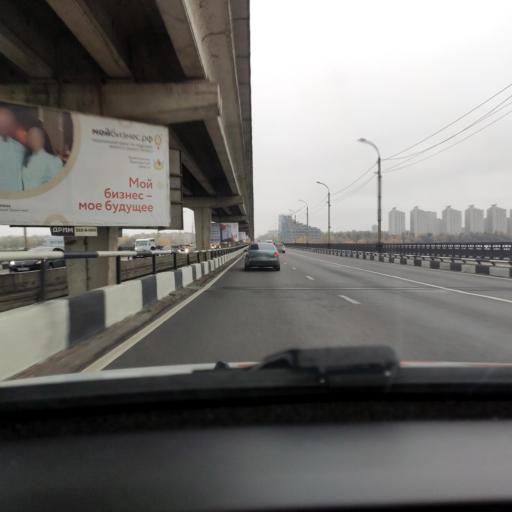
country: RU
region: Voronezj
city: Voronezh
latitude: 51.6938
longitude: 39.2407
